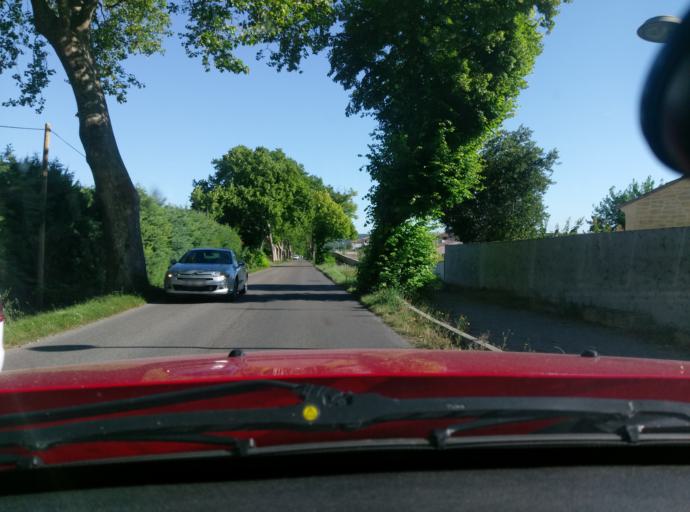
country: FR
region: Languedoc-Roussillon
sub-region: Departement du Gard
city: Uzes
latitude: 44.0230
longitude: 4.4143
